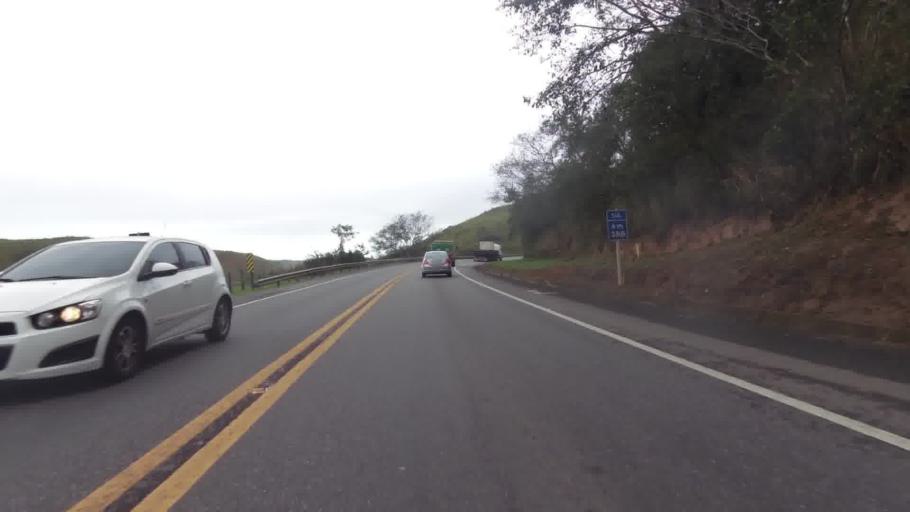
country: BR
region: Espirito Santo
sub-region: Rio Novo Do Sul
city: Rio Novo do Sul
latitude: -20.8561
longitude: -40.8776
